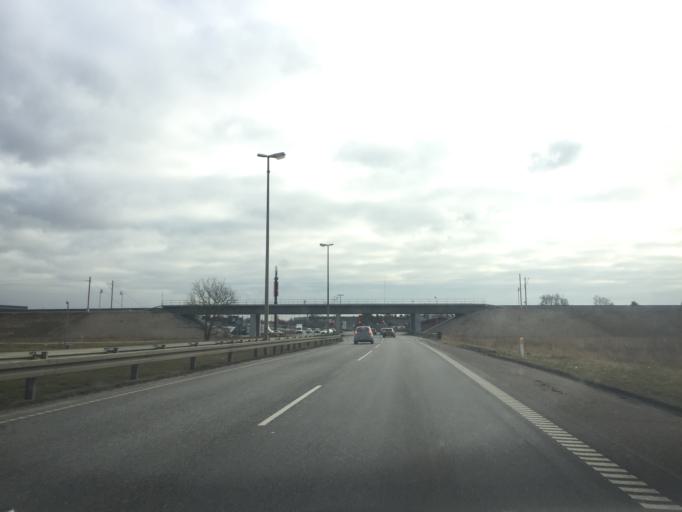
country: DK
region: Capital Region
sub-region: Ishoj Kommune
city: Ishoj
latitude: 55.6239
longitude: 12.3177
